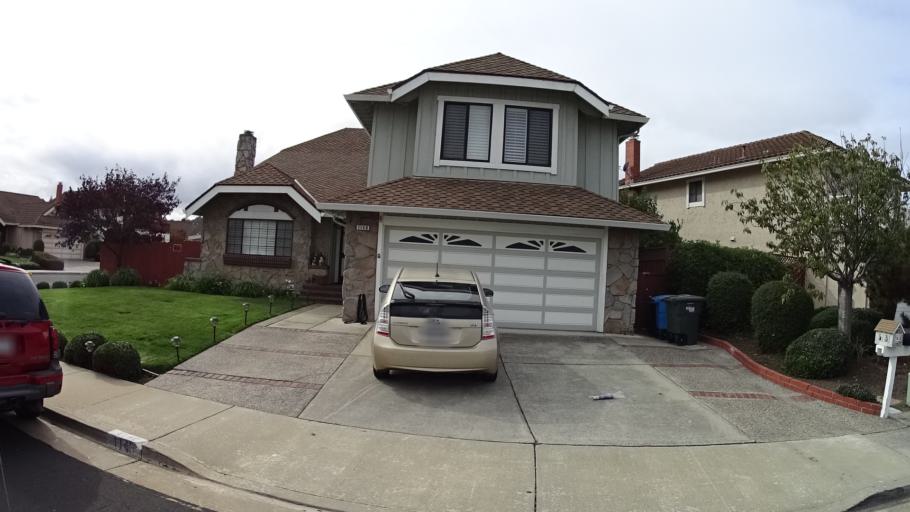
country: US
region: California
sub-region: San Mateo County
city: Belmont
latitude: 37.5333
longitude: -122.2790
